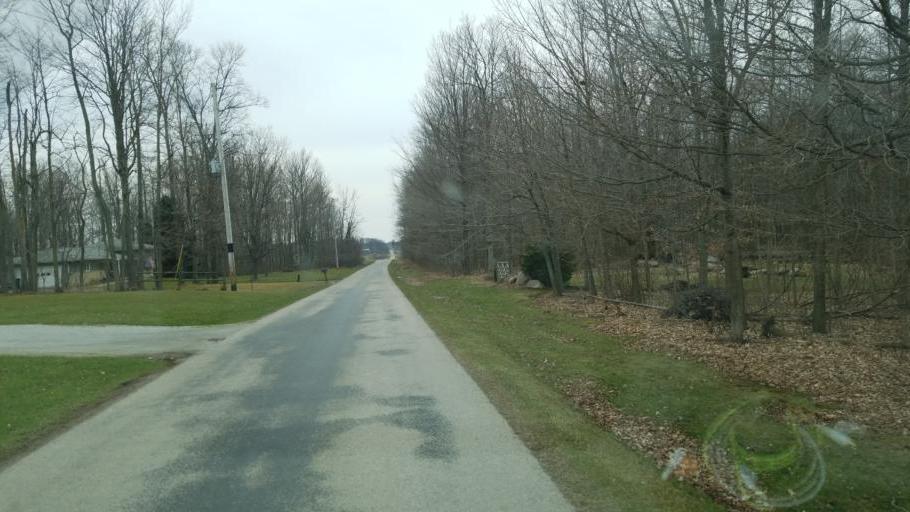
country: US
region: Ohio
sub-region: Huron County
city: Greenwich
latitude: 41.0993
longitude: -82.5632
